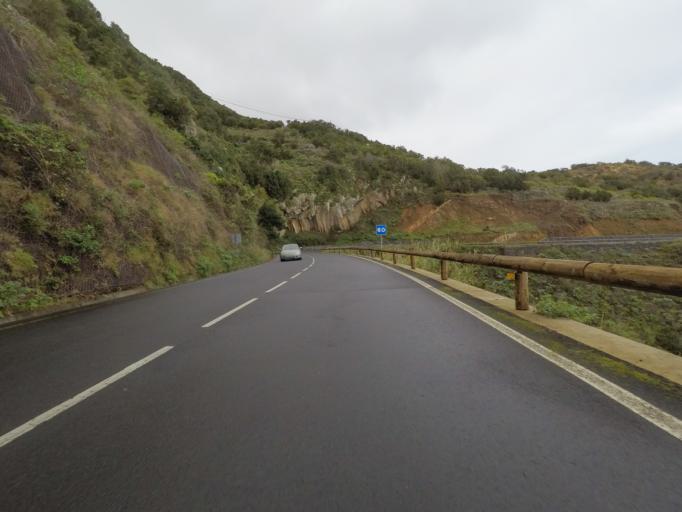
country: ES
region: Canary Islands
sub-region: Provincia de Santa Cruz de Tenerife
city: Agulo
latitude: 28.1895
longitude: -17.2268
